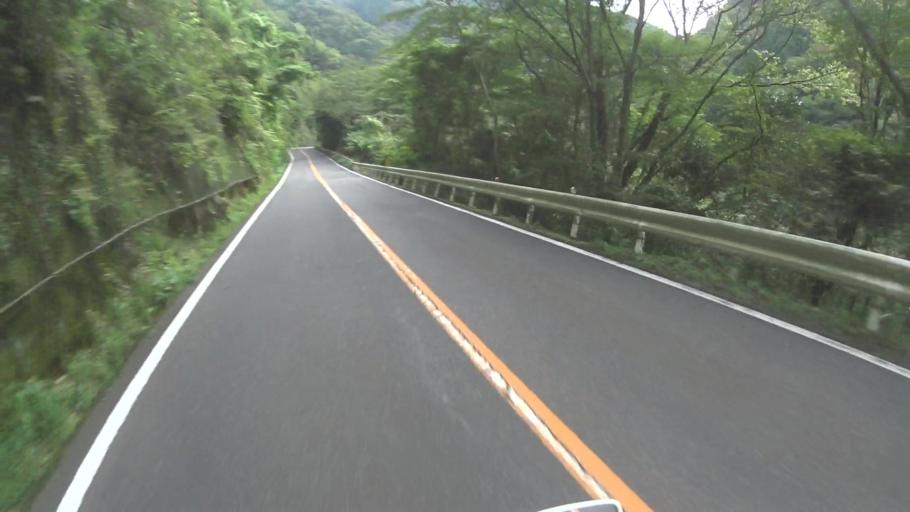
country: JP
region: Kyoto
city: Uji
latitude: 34.8955
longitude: 135.8684
